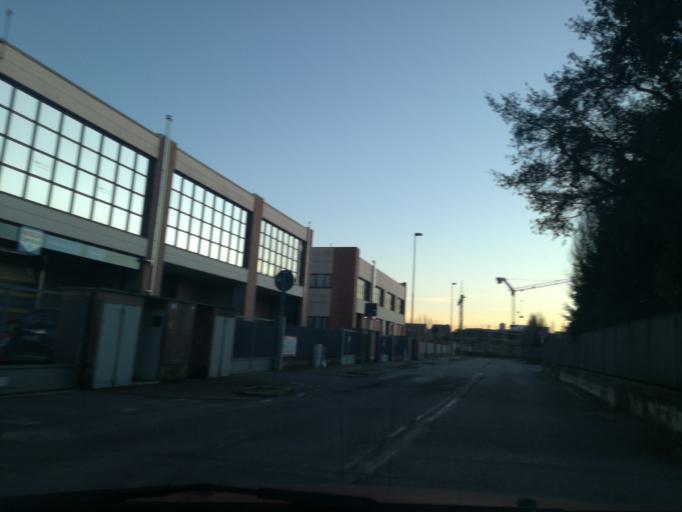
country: IT
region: Lombardy
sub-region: Provincia di Lecco
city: Osnago
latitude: 45.6712
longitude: 9.3947
